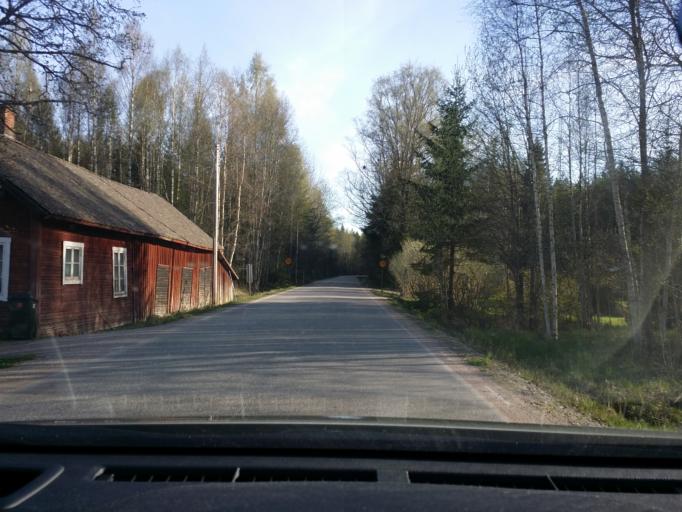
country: SE
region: Dalarna
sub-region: Avesta Kommun
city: Avesta
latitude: 60.0702
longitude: 16.3492
